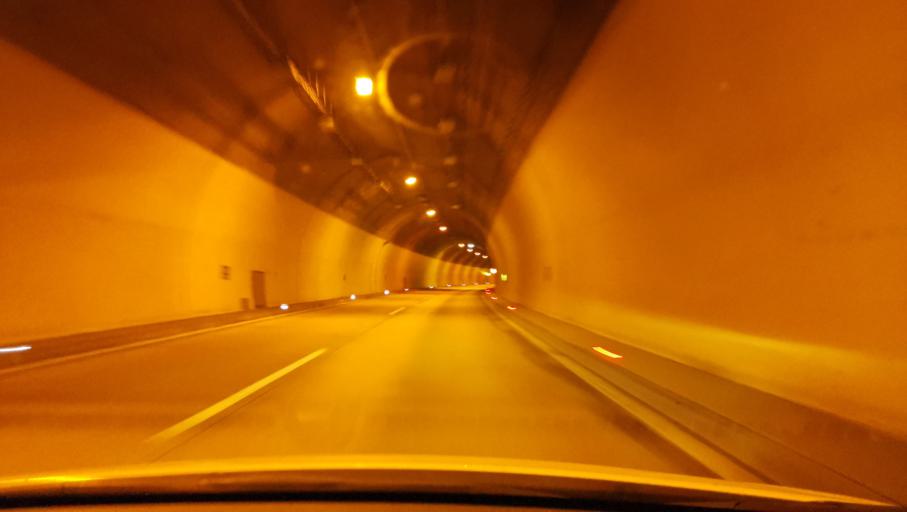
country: AT
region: Styria
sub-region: Politischer Bezirk Graz-Umgebung
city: Deutschfeistritz
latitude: 47.1925
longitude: 15.3275
